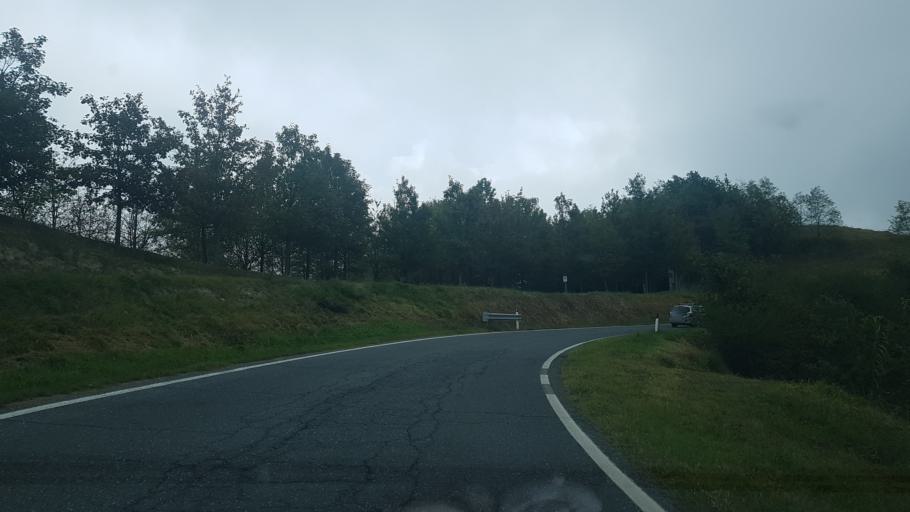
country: IT
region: Piedmont
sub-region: Provincia di Cuneo
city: Paroldo
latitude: 44.4324
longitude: 8.0786
